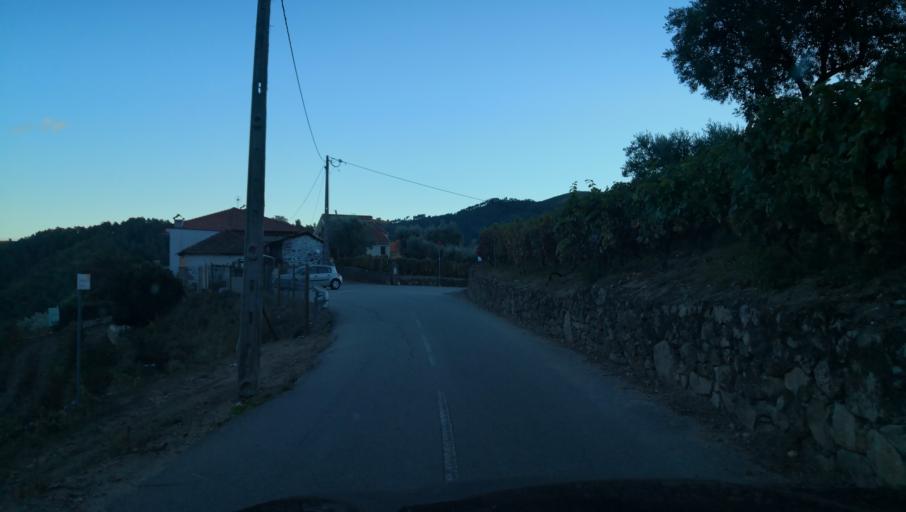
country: PT
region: Vila Real
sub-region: Santa Marta de Penaguiao
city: Santa Marta de Penaguiao
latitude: 41.2563
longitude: -7.8039
